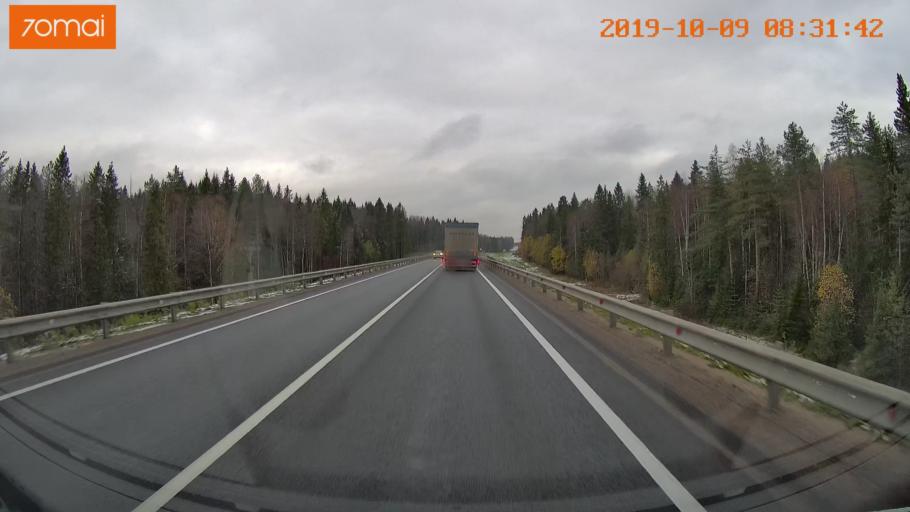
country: RU
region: Vologda
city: Gryazovets
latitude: 58.8573
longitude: 40.2003
